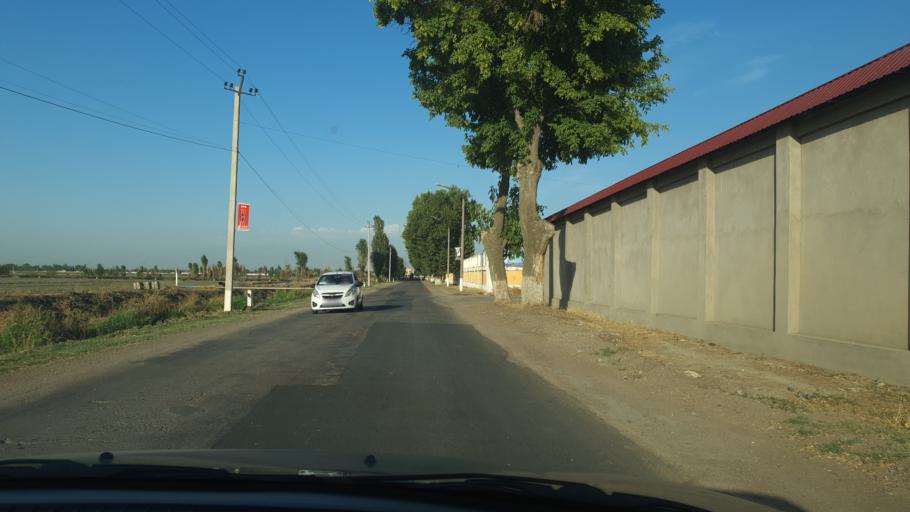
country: UZ
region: Toshkent
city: Tuytepa
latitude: 41.0850
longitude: 69.3386
